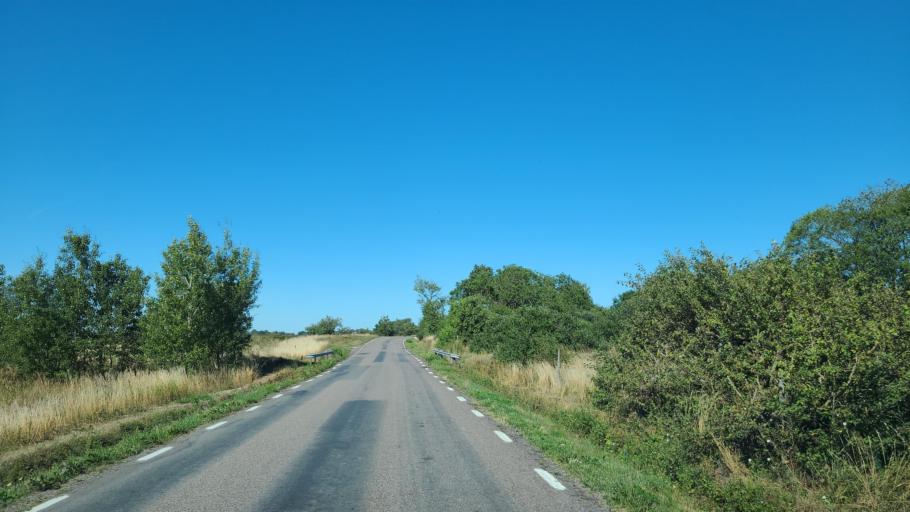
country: SE
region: Kalmar
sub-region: Borgholms Kommun
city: Borgholm
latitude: 56.8555
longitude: 16.8106
